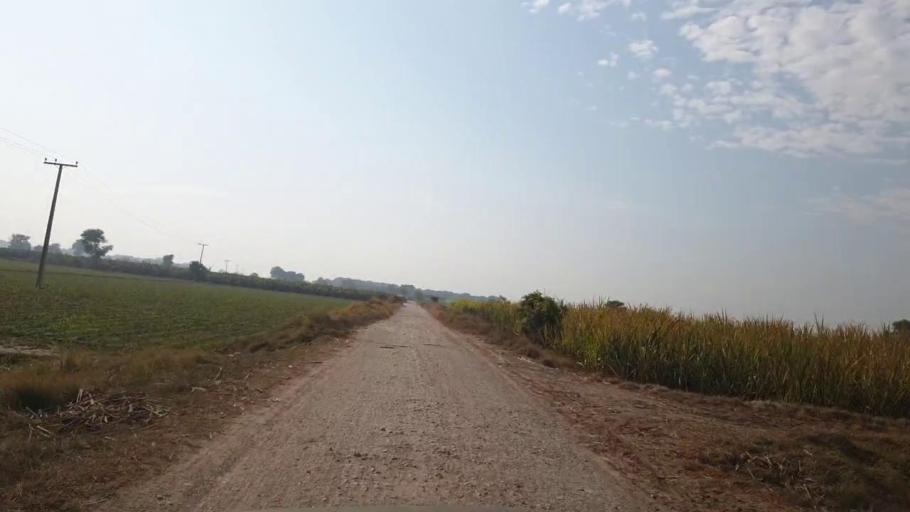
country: PK
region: Sindh
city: Matiari
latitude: 25.5635
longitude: 68.5200
